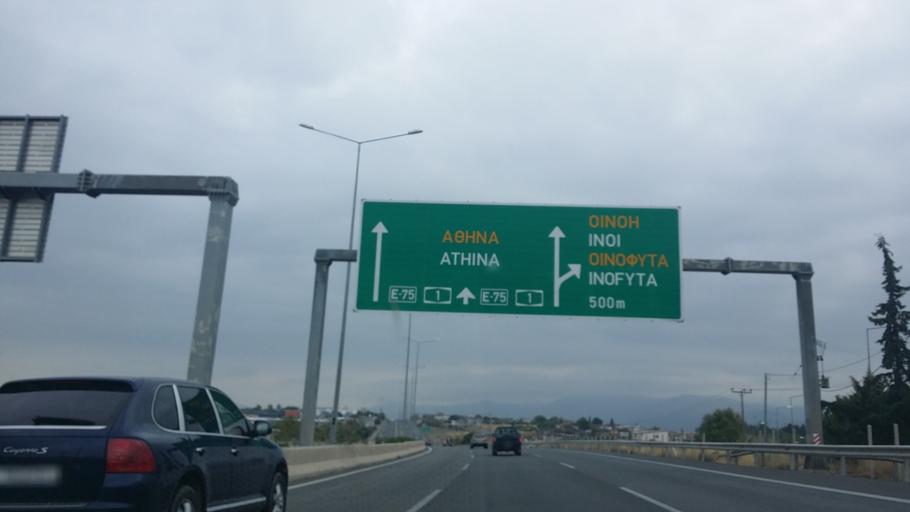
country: GR
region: Central Greece
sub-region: Nomos Voiotias
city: Schimatari
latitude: 38.3304
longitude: 23.6035
